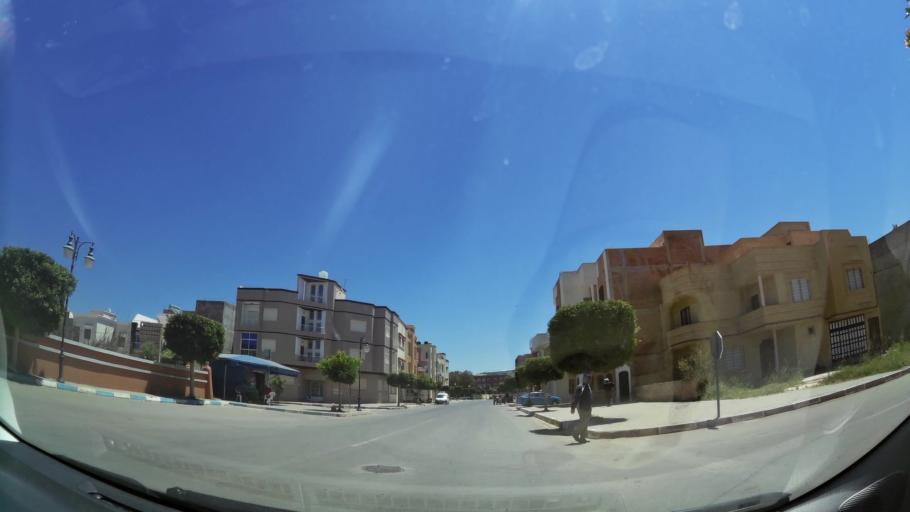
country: MA
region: Oriental
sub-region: Berkane-Taourirt
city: Madagh
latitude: 35.0792
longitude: -2.2289
